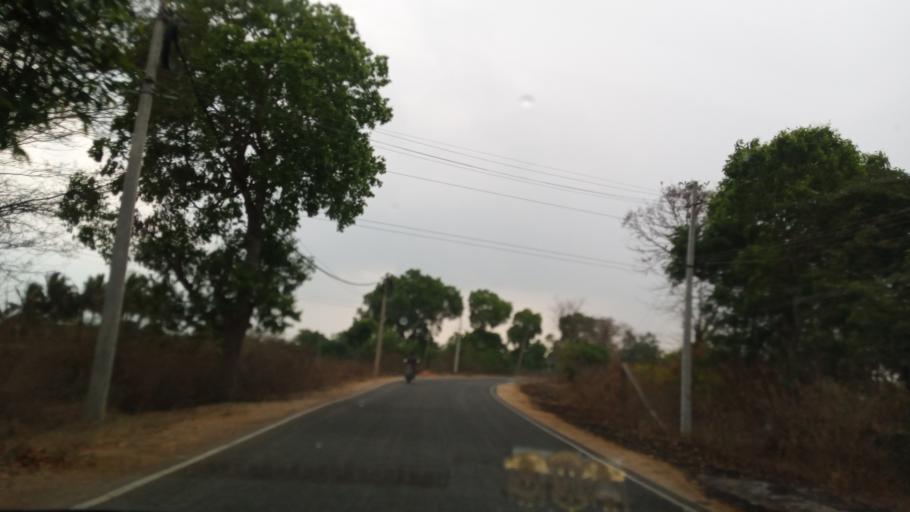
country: IN
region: Karnataka
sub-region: Kolar
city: Mulbagal
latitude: 13.1190
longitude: 78.3378
